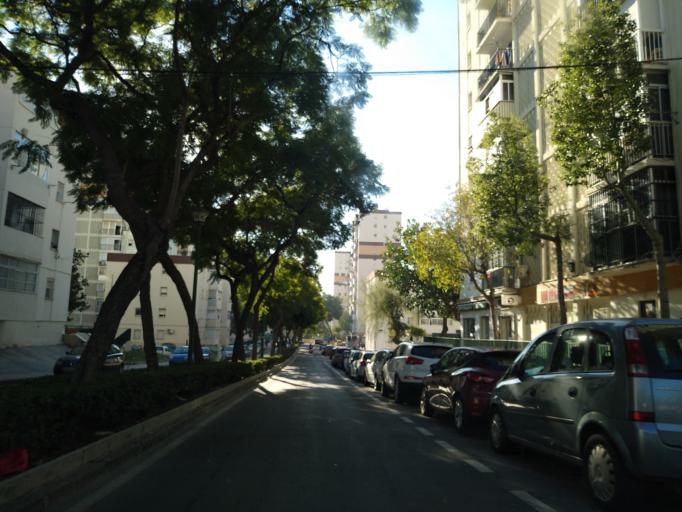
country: ES
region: Andalusia
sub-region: Provincia de Malaga
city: Malaga
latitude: 36.7397
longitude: -4.4327
